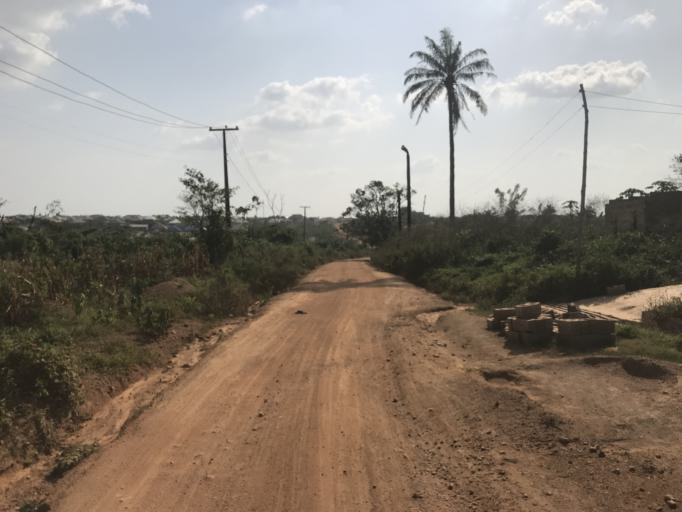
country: NG
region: Osun
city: Osogbo
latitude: 7.8221
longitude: 4.5656
